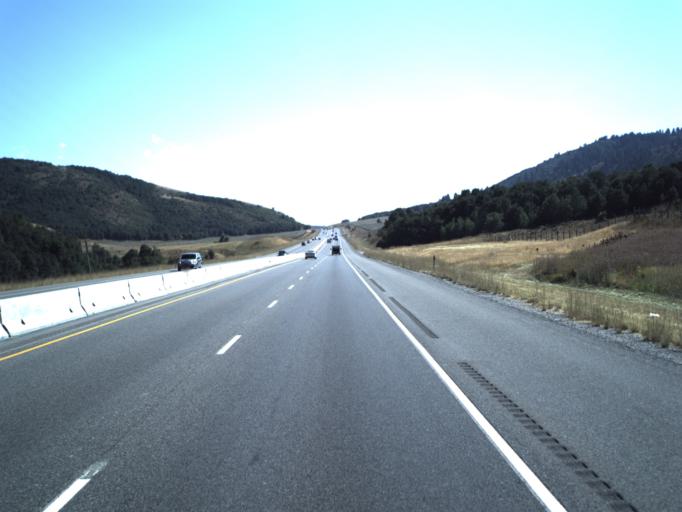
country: US
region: Utah
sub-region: Cache County
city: Wellsville
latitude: 41.5932
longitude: -111.9780
